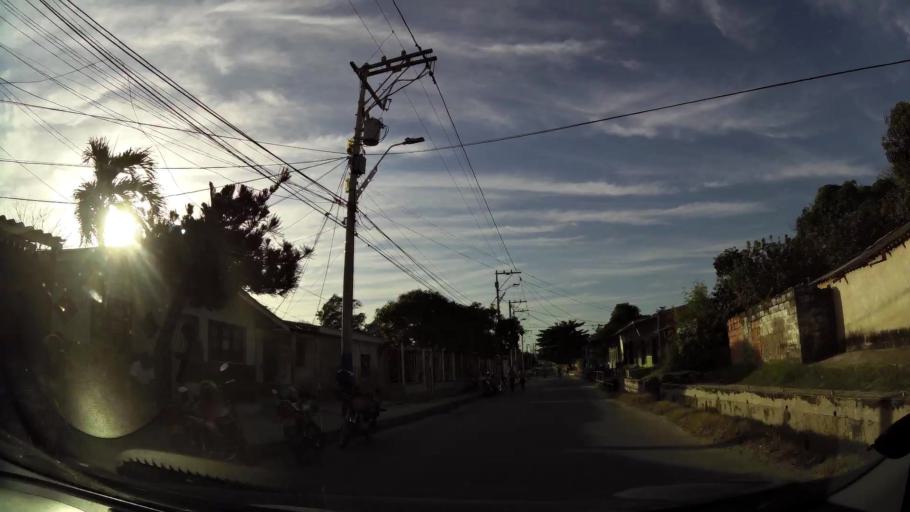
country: CO
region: Atlantico
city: Barranquilla
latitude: 10.9539
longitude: -74.8142
